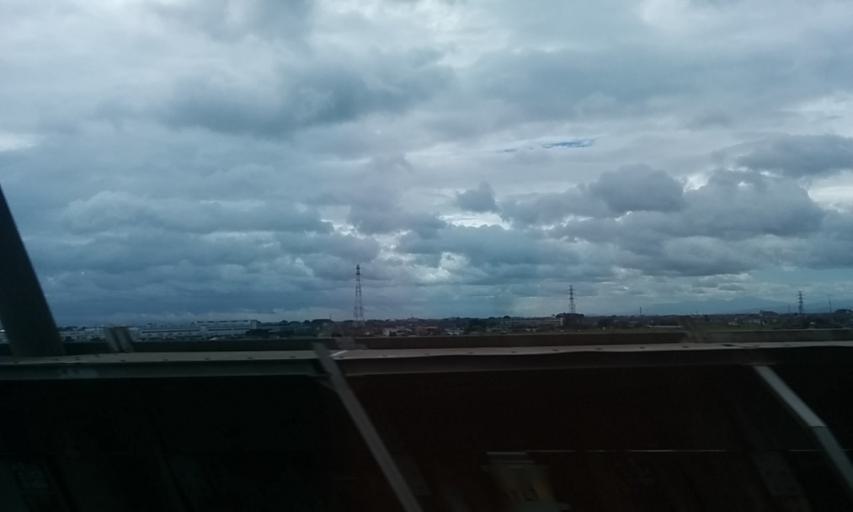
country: JP
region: Saitama
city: Kurihashi
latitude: 36.1223
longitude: 139.7136
